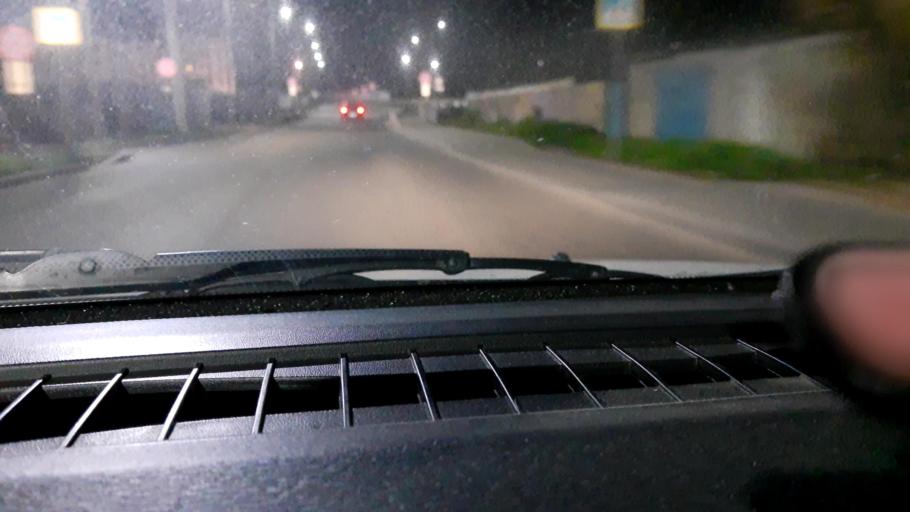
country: RU
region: Nizjnij Novgorod
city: Burevestnik
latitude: 56.2107
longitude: 43.8247
